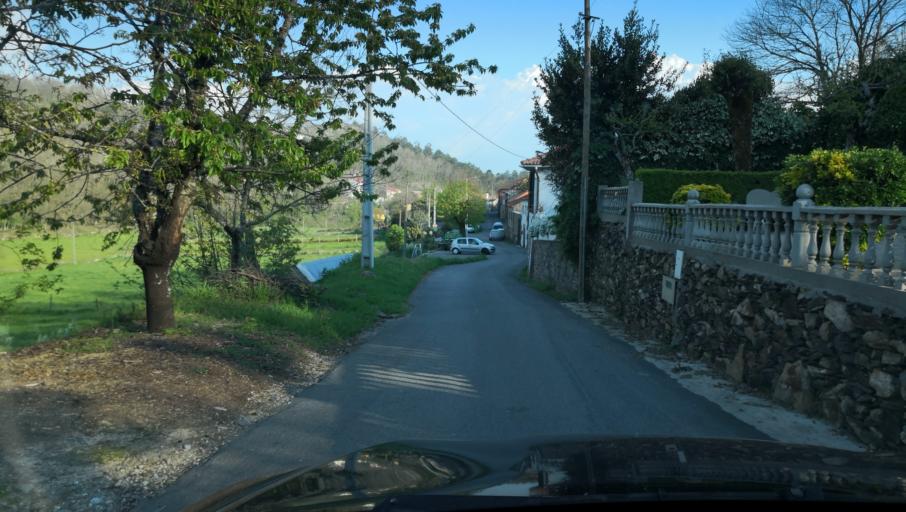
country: PT
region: Vila Real
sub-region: Vila Real
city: Vila Real
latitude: 41.3010
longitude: -7.8382
